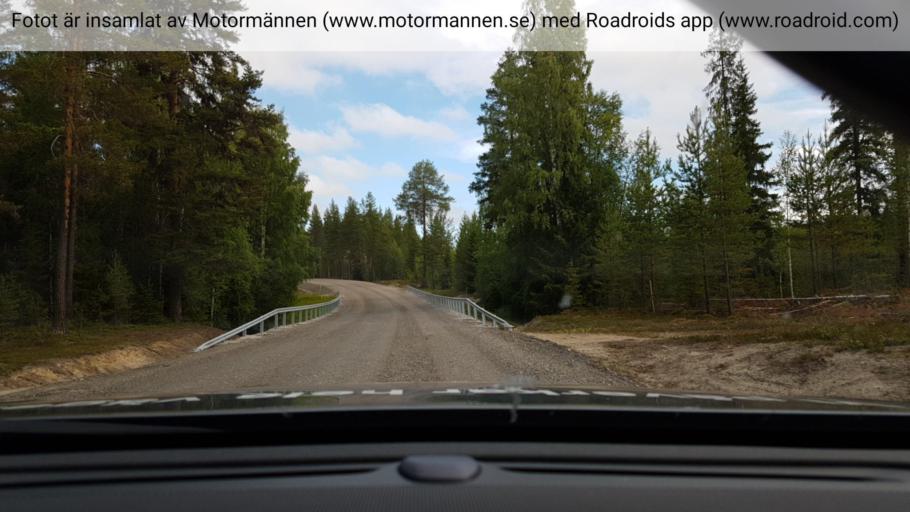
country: SE
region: Vaesterbotten
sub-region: Norsjo Kommun
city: Norsjoe
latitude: 64.6322
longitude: 19.2887
